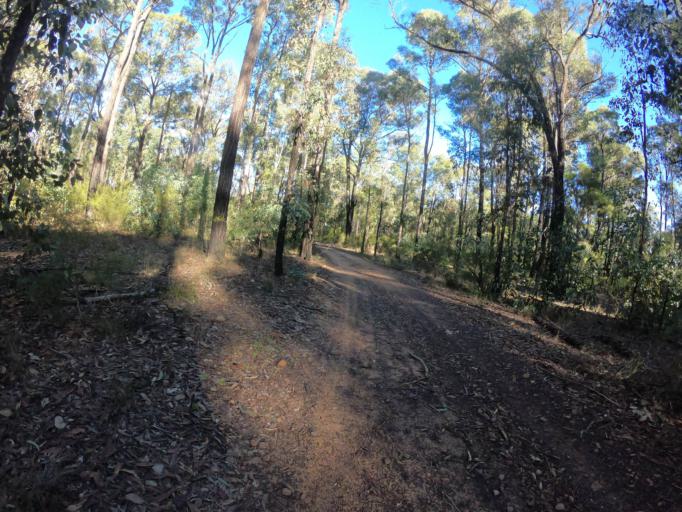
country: AU
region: New South Wales
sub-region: Hawkesbury
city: South Windsor
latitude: -33.6504
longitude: 150.8035
